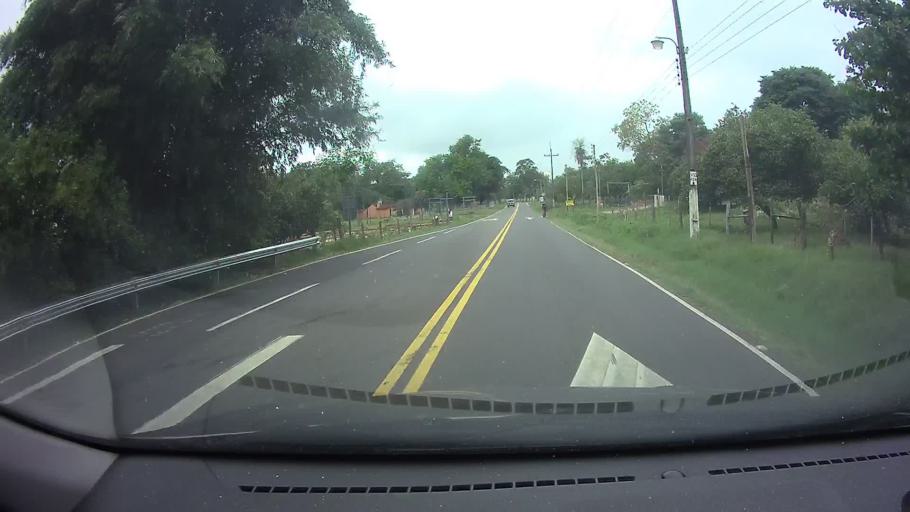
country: PY
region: Central
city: Nueva Italia
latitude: -25.6050
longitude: -57.4125
